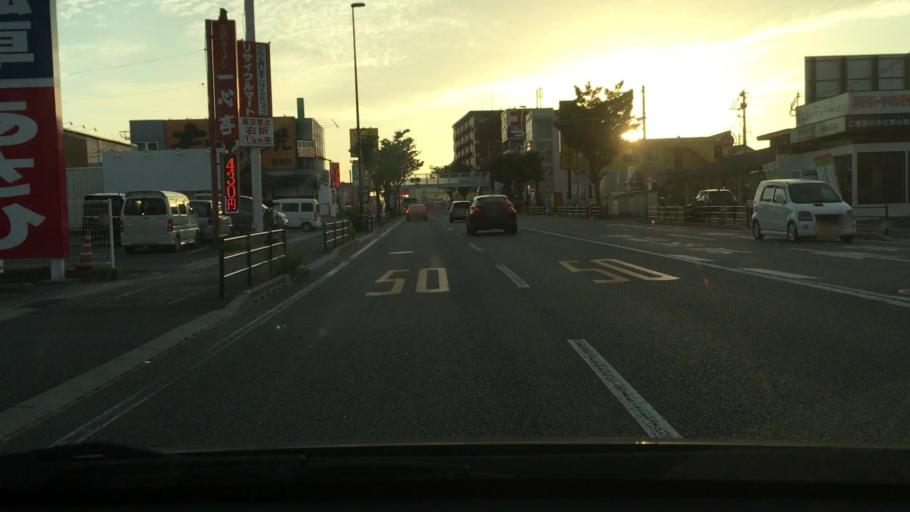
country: JP
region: Fukuoka
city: Fukuoka-shi
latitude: 33.5680
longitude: 130.3351
